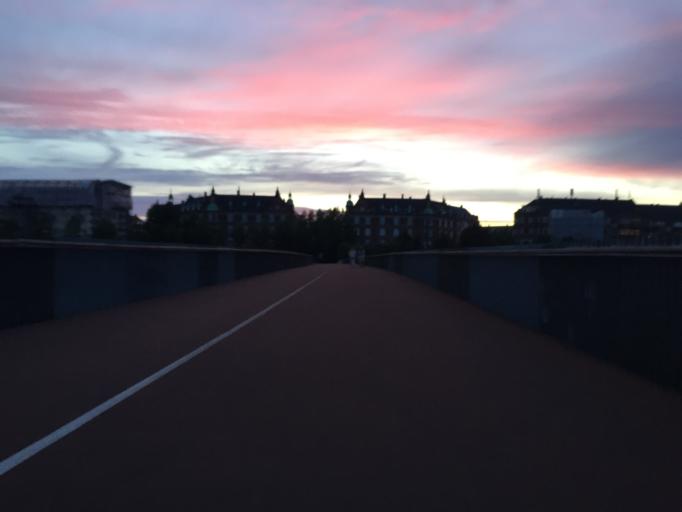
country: DK
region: Capital Region
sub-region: Kobenhavn
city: Christianshavn
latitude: 55.6948
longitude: 12.5930
